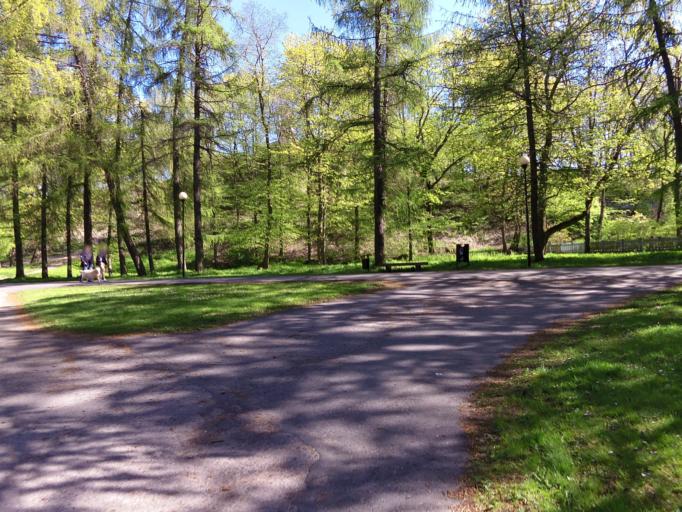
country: EE
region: Harju
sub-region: Tallinna linn
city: Tallinn
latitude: 59.4380
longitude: 24.7970
